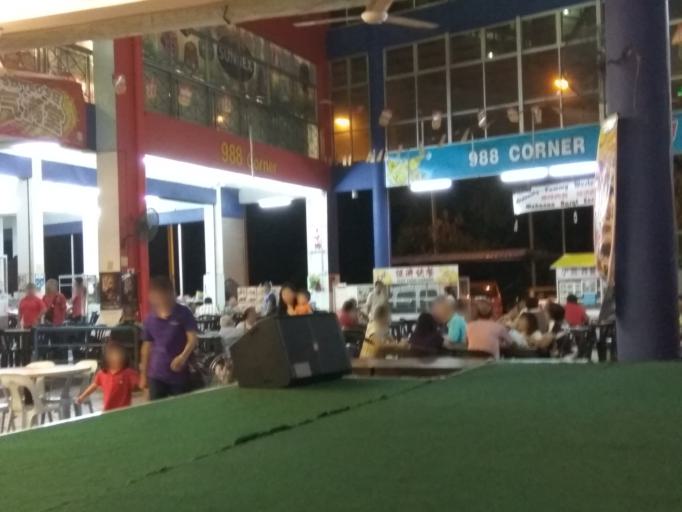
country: MY
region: Sarawak
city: Sibu
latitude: 2.2658
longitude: 111.8593
